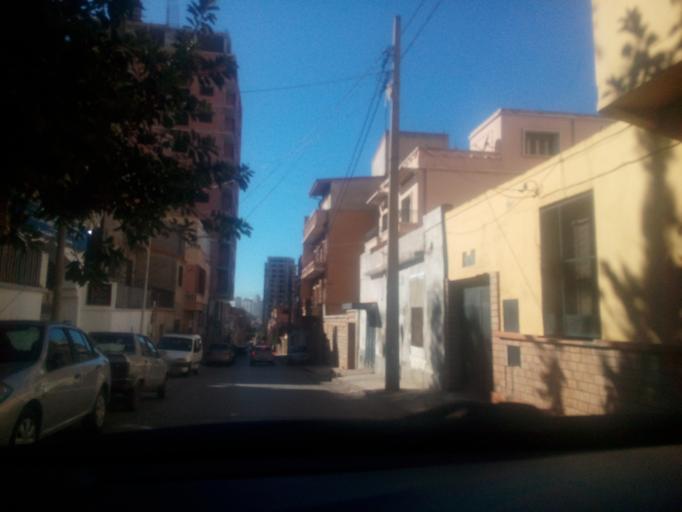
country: DZ
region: Oran
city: Oran
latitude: 35.7135
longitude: -0.6180
